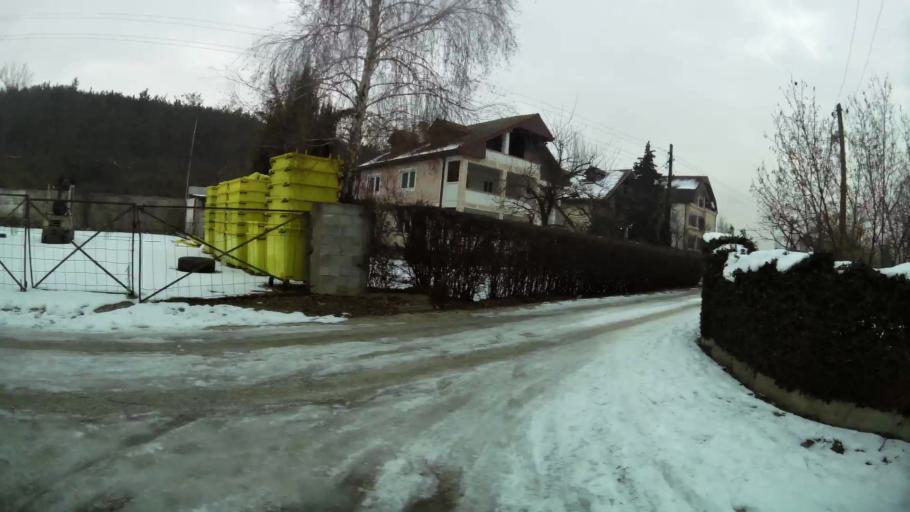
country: MK
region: Saraj
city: Saraj
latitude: 42.0099
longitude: 21.3316
